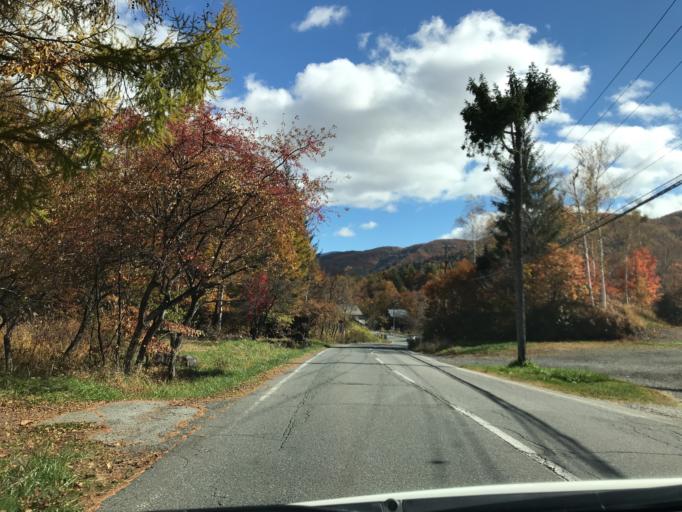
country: JP
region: Nagano
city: Toyoshina
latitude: 36.1240
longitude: 137.6411
